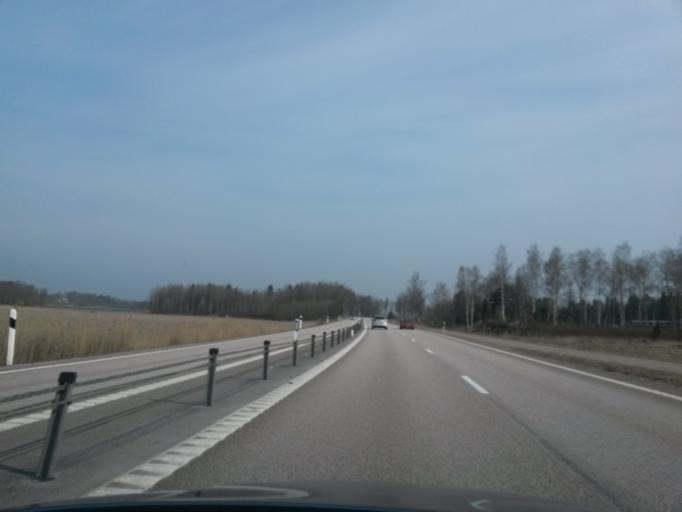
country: SE
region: Vaestra Goetaland
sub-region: Mariestads Kommun
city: Mariestad
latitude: 58.7581
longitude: 13.9682
